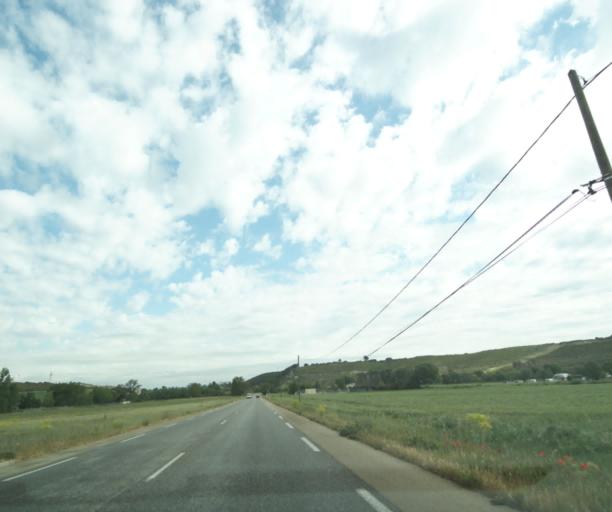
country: FR
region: Provence-Alpes-Cote d'Azur
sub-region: Departement des Bouches-du-Rhone
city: Cabries
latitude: 43.4734
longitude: 5.3551
